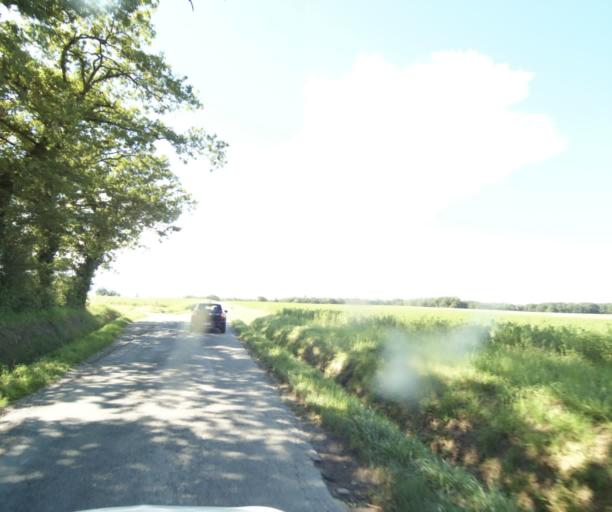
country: FR
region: Rhone-Alpes
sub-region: Departement de la Haute-Savoie
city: Douvaine
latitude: 46.3274
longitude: 6.3130
